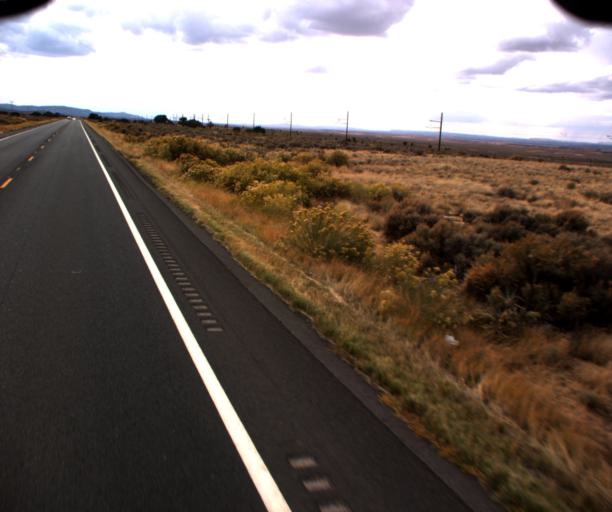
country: US
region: Arizona
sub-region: Navajo County
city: Kayenta
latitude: 36.5130
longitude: -110.5993
